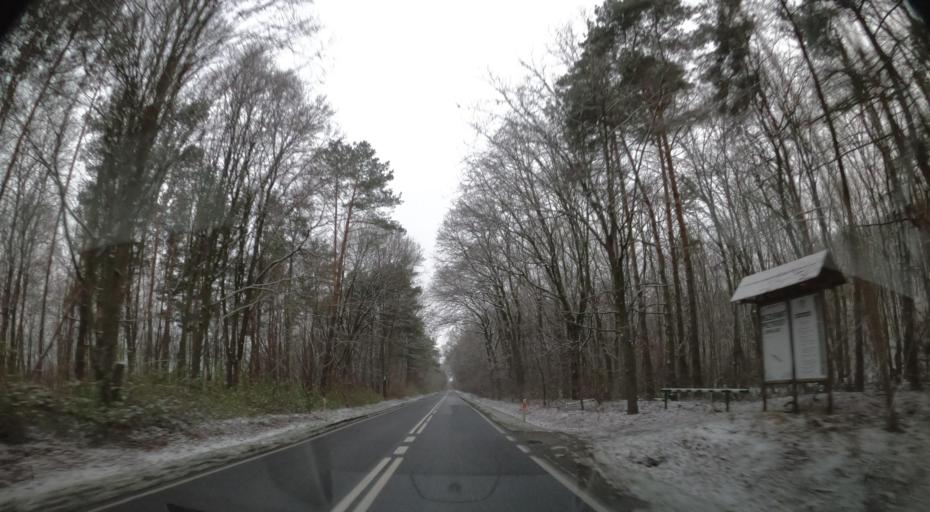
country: PL
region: Masovian Voivodeship
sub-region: Powiat plocki
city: Maszewo Duze
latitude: 52.5733
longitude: 19.5597
